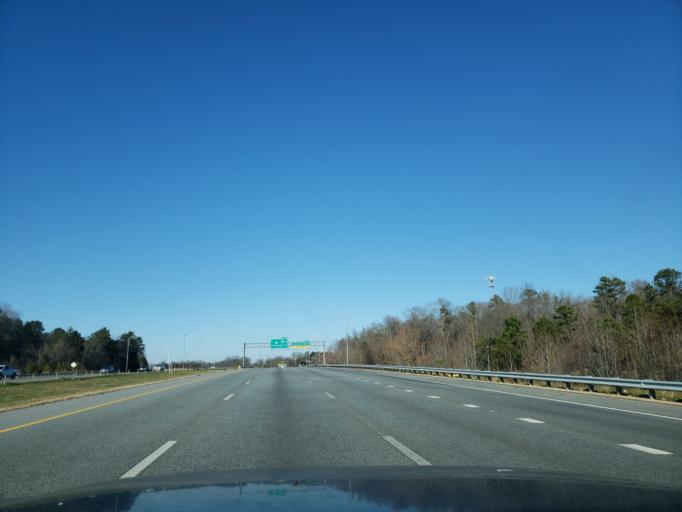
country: US
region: North Carolina
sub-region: Guilford County
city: High Point
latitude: 35.9774
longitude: -79.9740
